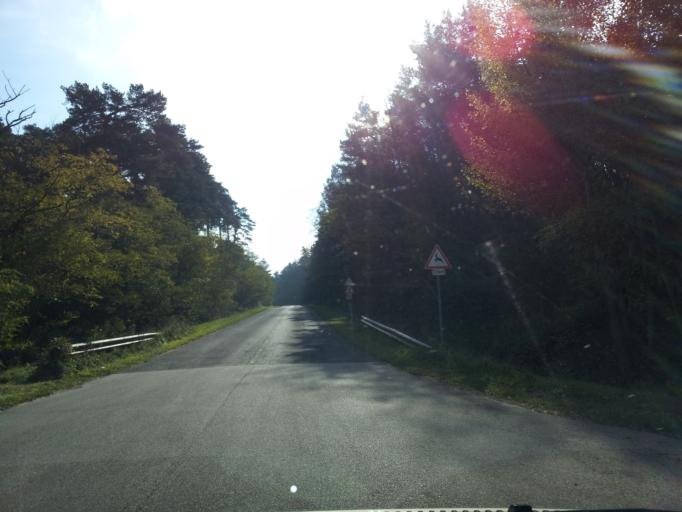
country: HU
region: Gyor-Moson-Sopron
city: Bakonyszentlaszlo
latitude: 47.3780
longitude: 17.8082
